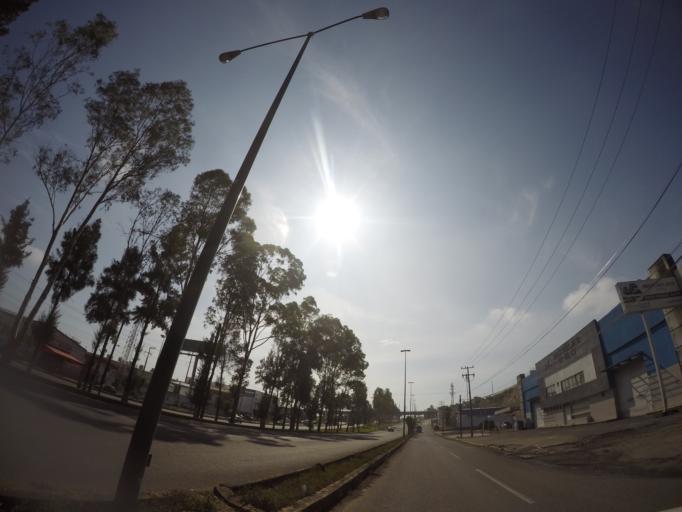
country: MX
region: Michoacan
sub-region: Tarimbaro
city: Real Hacienda (Metropolis)
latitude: 19.7247
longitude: -101.1993
